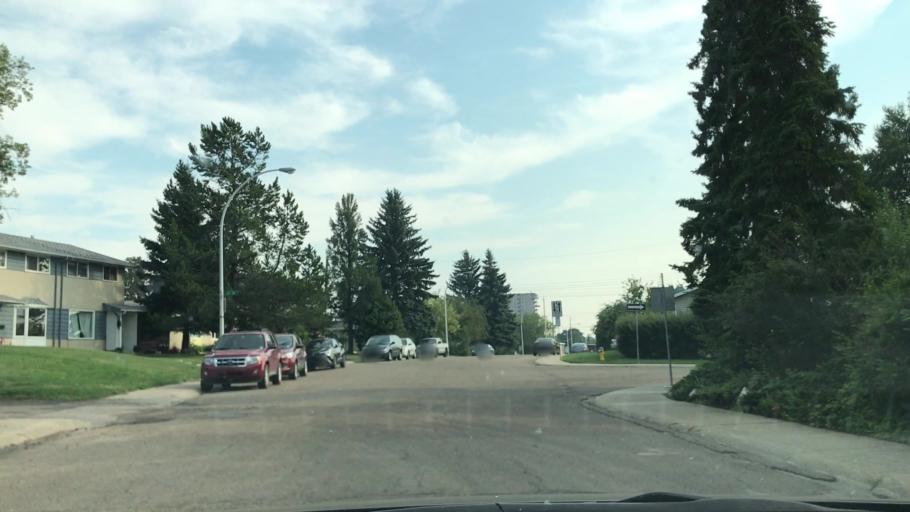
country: CA
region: Alberta
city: Edmonton
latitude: 53.4898
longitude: -113.5081
